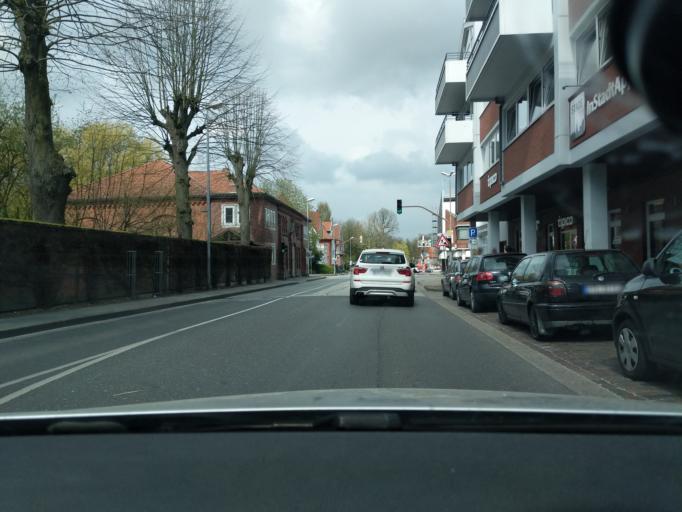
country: DE
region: Lower Saxony
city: Stade
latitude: 53.5994
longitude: 9.4734
